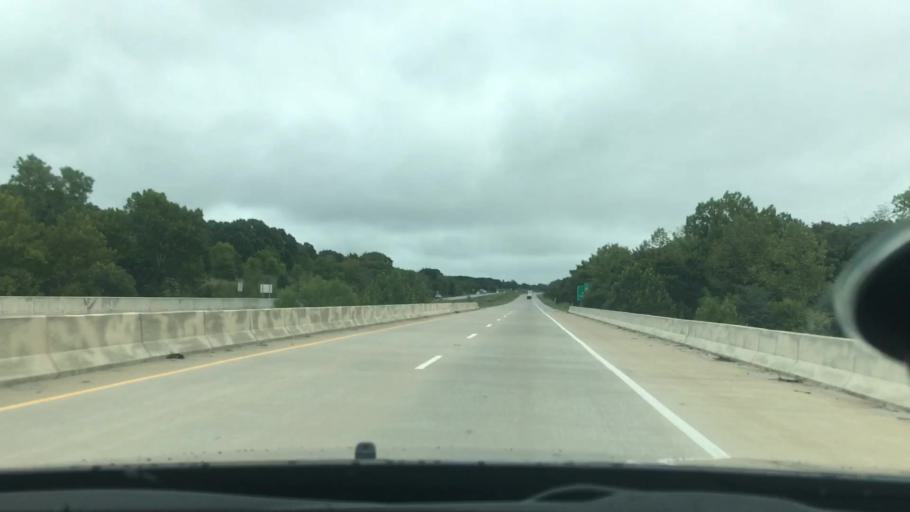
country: US
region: Oklahoma
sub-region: Okfuskee County
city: Okemah
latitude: 35.3951
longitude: -96.3984
